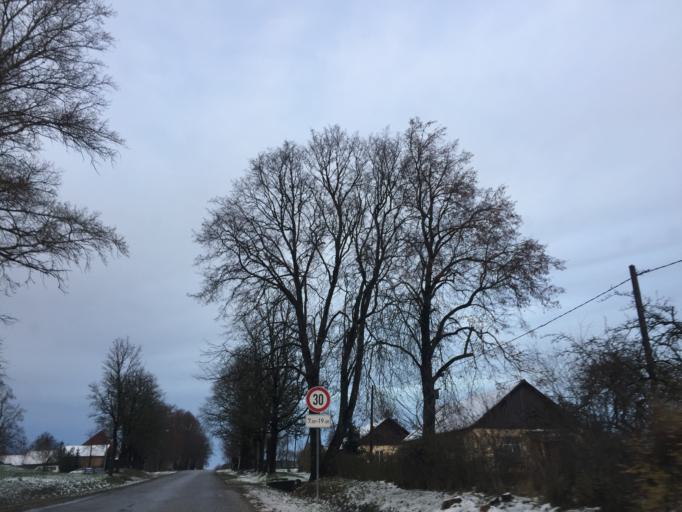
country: LV
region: Limbazu Rajons
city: Limbazi
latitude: 57.5937
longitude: 24.8500
